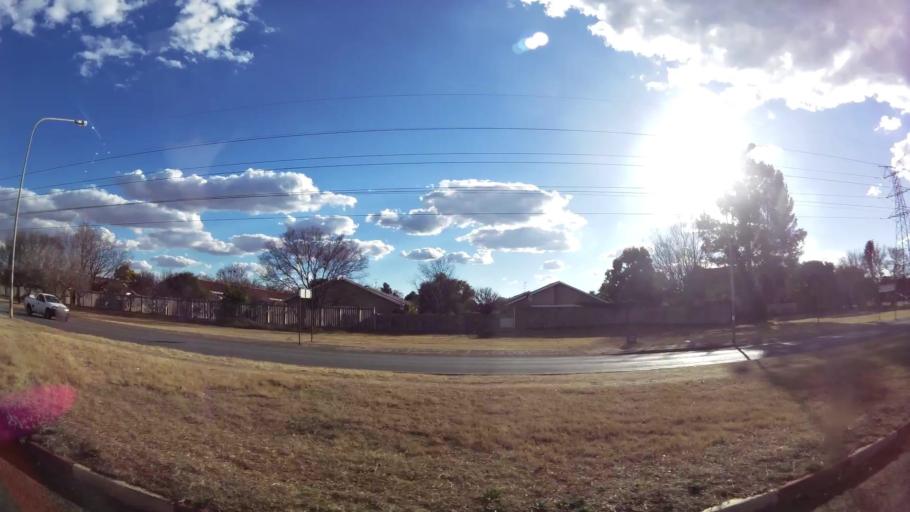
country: ZA
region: North-West
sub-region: Dr Kenneth Kaunda District Municipality
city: Potchefstroom
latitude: -26.7079
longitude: 27.1040
